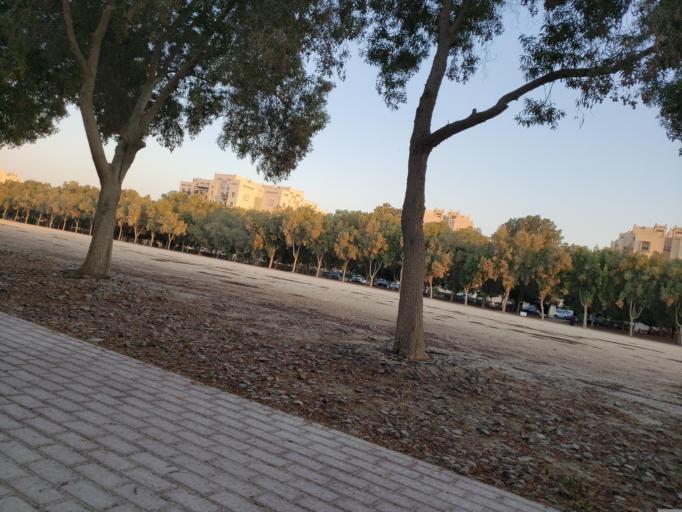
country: AE
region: Dubai
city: Dubai
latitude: 25.0065
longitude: 55.2459
